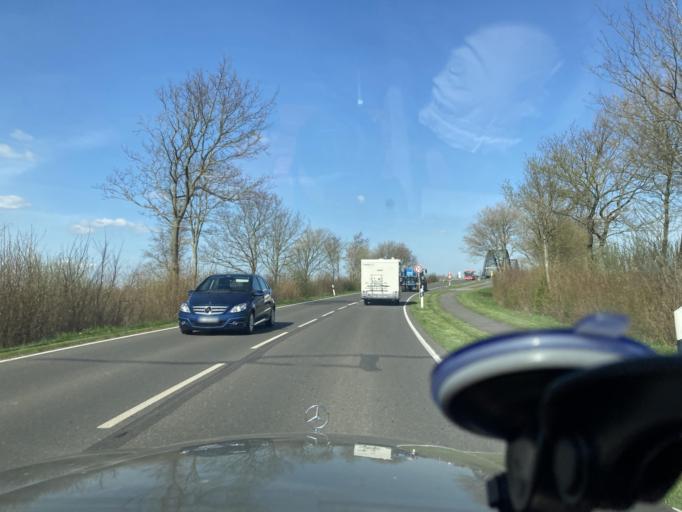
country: DE
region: Schleswig-Holstein
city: Friedrichstadt
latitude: 54.3658
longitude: 9.0907
